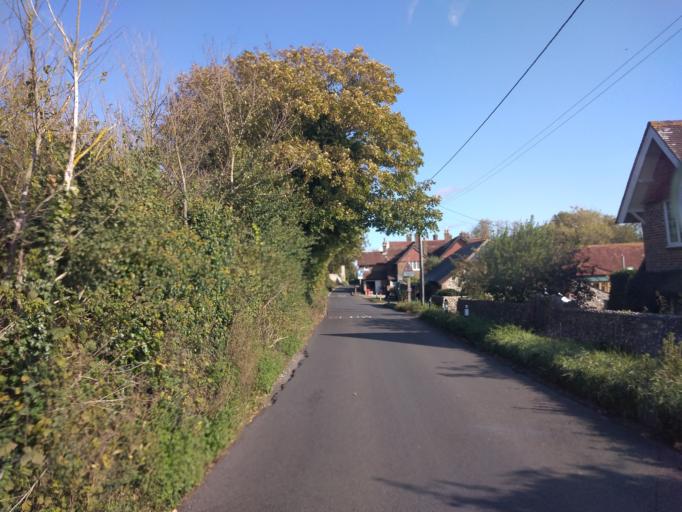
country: GB
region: England
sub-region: East Sussex
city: Seaford
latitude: 50.7964
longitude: 0.1515
